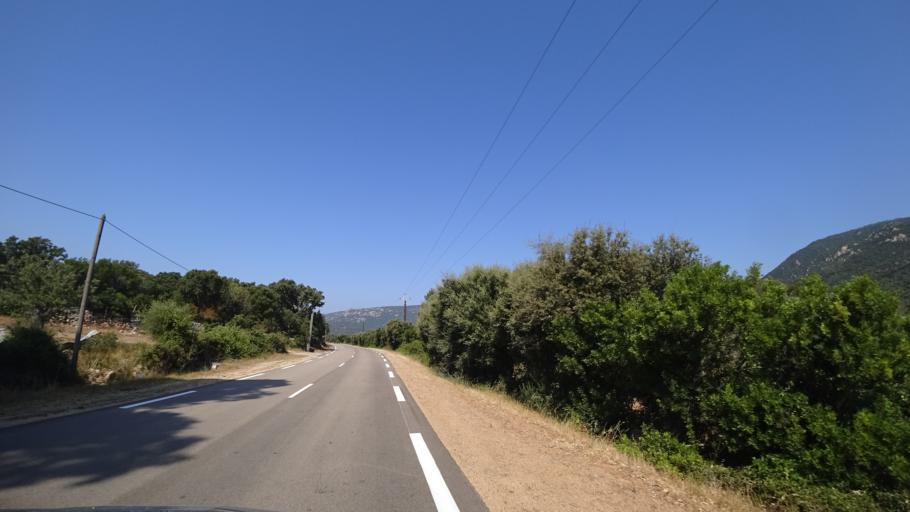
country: FR
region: Corsica
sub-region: Departement de la Corse-du-Sud
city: Sartene
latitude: 41.5027
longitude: 9.0265
